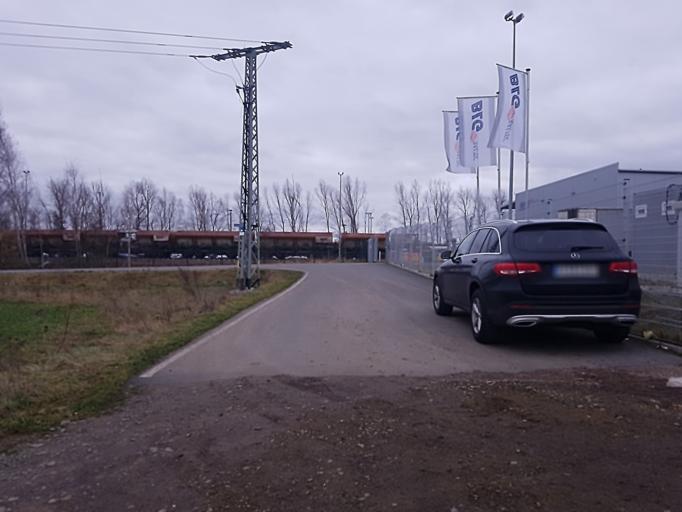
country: DE
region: Brandenburg
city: Falkenberg
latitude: 51.5860
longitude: 13.2855
